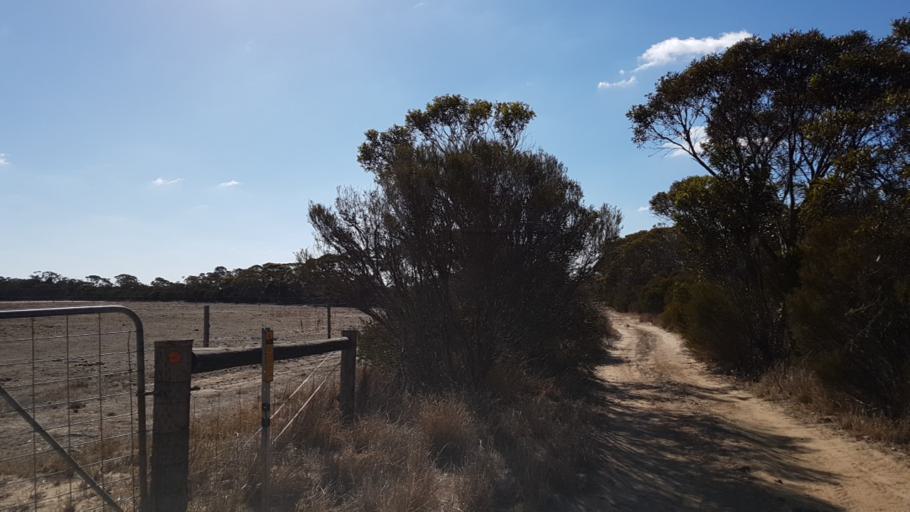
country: AU
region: South Australia
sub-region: Alexandrina
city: Strathalbyn
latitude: -35.3767
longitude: 138.8335
